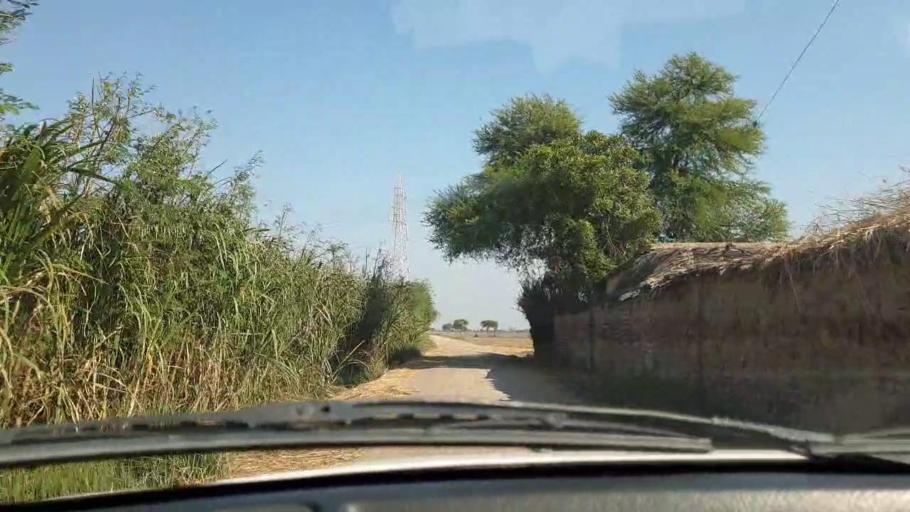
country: PK
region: Sindh
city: Bulri
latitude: 24.8423
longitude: 68.3385
